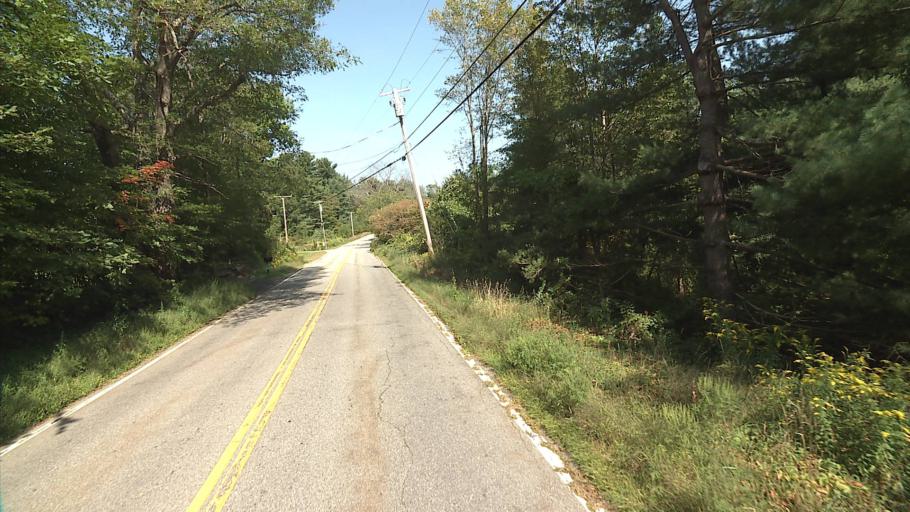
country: US
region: Connecticut
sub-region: Windham County
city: Quinebaug
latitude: 42.0038
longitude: -72.0004
